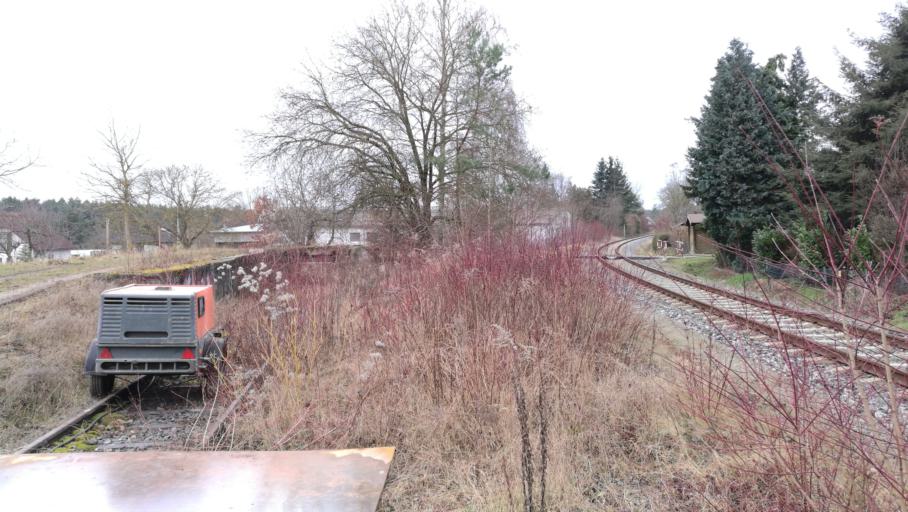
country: DE
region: Bavaria
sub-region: Regierungsbezirk Mittelfranken
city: Hilpoltstein
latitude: 49.1888
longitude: 11.1817
